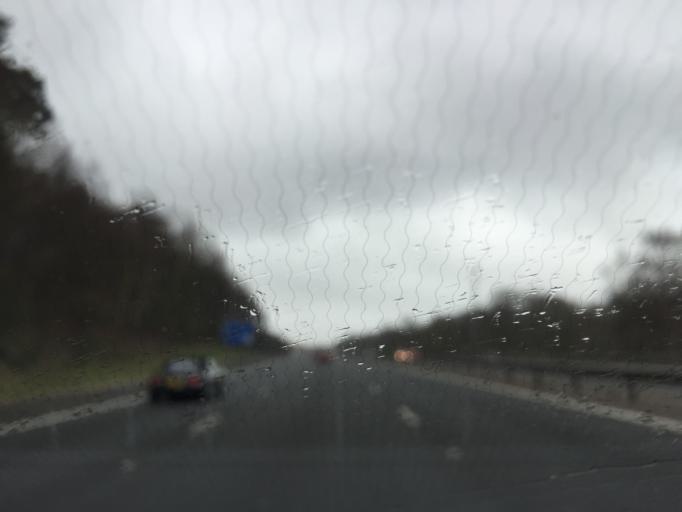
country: GB
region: England
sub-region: Hampshire
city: Bursledon
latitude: 50.8812
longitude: -1.2822
